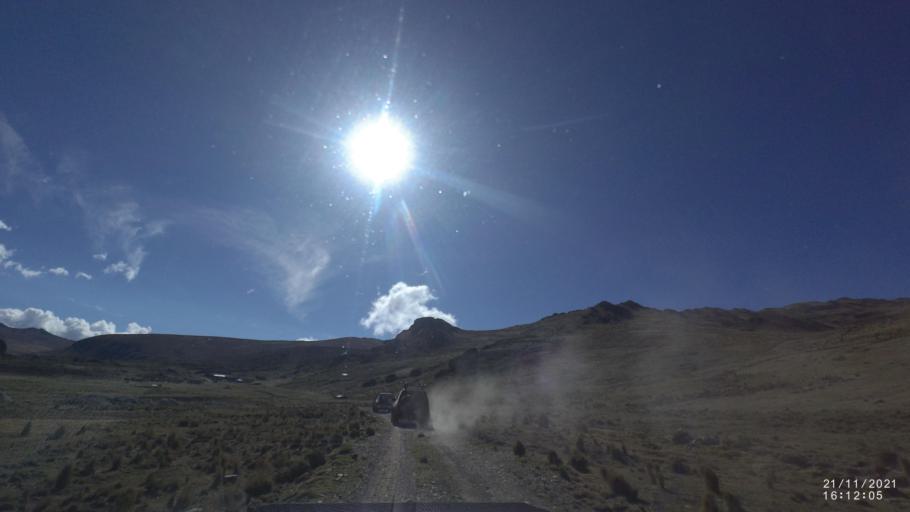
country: BO
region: Cochabamba
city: Cochabamba
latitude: -16.9956
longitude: -66.2730
